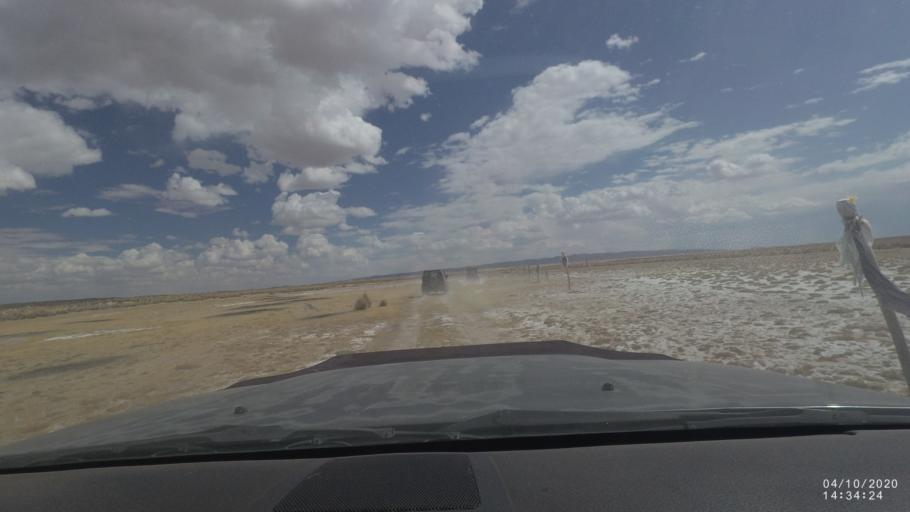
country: BO
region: Oruro
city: Poopo
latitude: -18.6709
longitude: -67.4692
